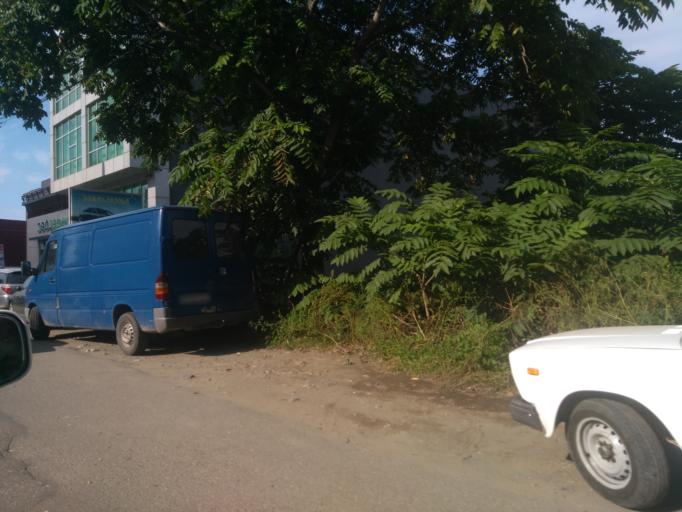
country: GE
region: Ajaria
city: Batumi
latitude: 41.6224
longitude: 41.6151
